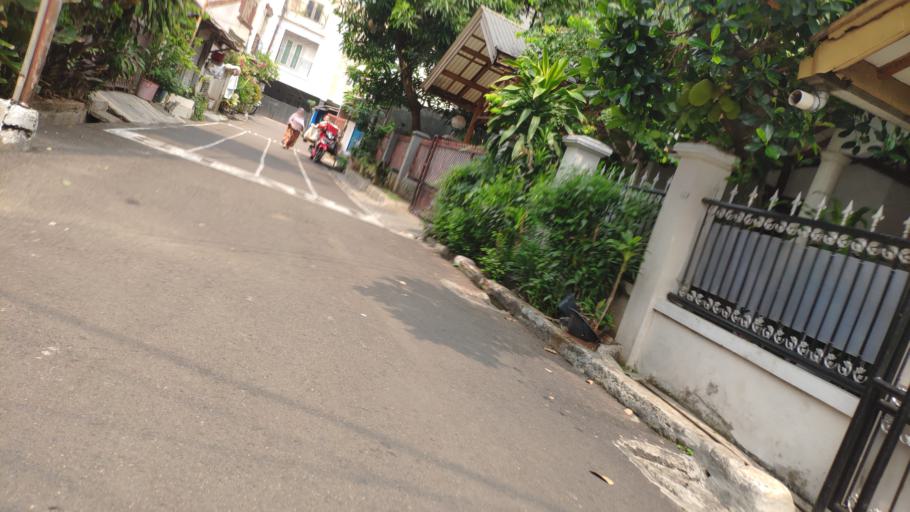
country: ID
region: Banten
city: South Tangerang
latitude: -6.2685
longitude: 106.7727
